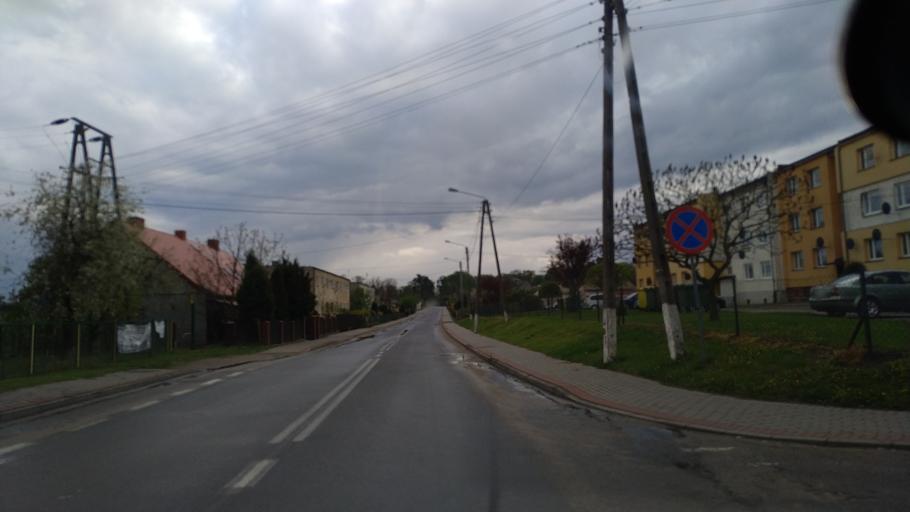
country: PL
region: Pomeranian Voivodeship
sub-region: Powiat starogardzki
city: Smetowo Graniczne
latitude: 53.7398
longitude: 18.6508
